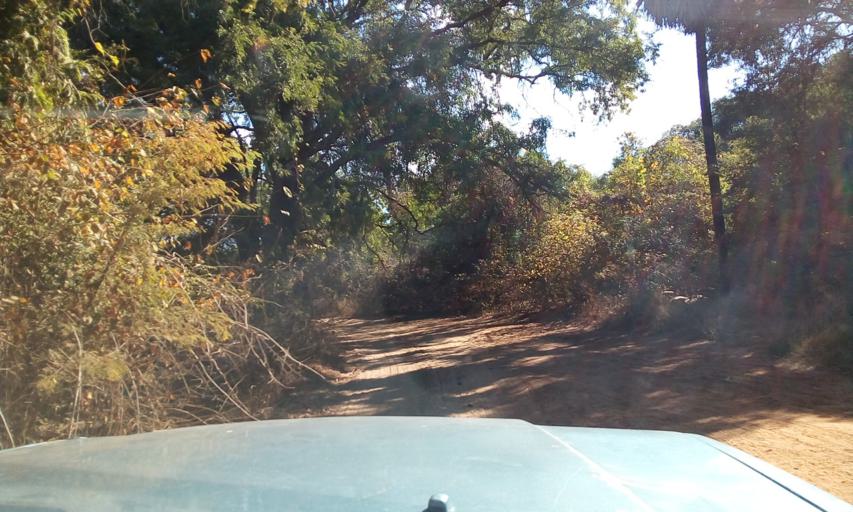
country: MG
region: Boeny
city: Mahajanga
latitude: -16.0623
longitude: 45.7936
